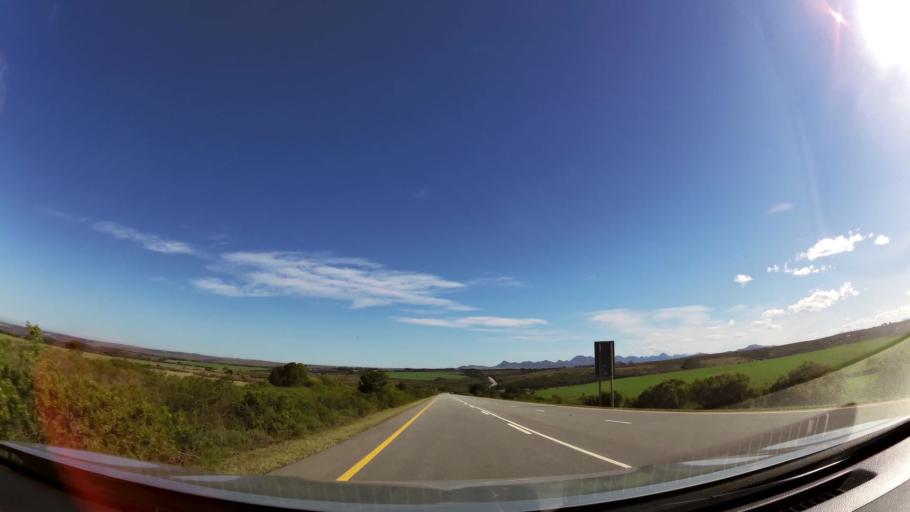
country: ZA
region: Eastern Cape
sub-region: Cacadu District Municipality
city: Kruisfontein
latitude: -34.0110
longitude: 24.6490
